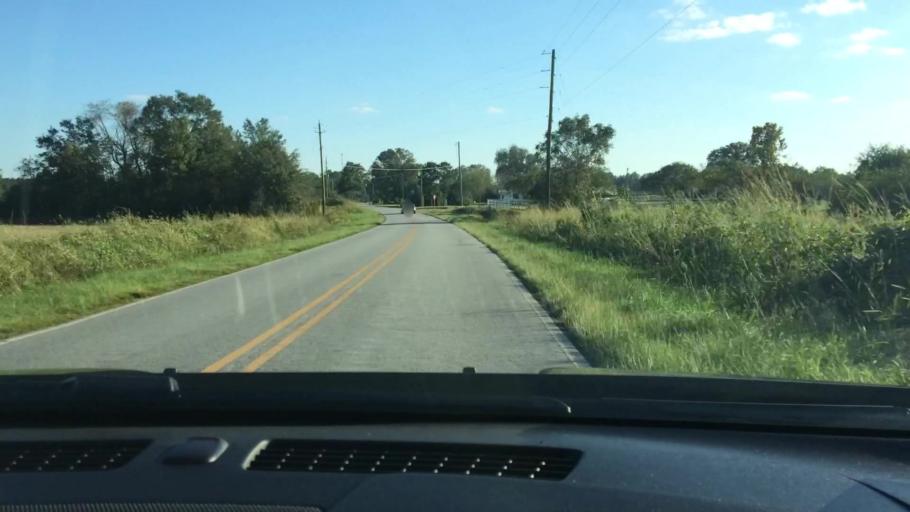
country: US
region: North Carolina
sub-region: Pitt County
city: Ayden
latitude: 35.5058
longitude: -77.4345
